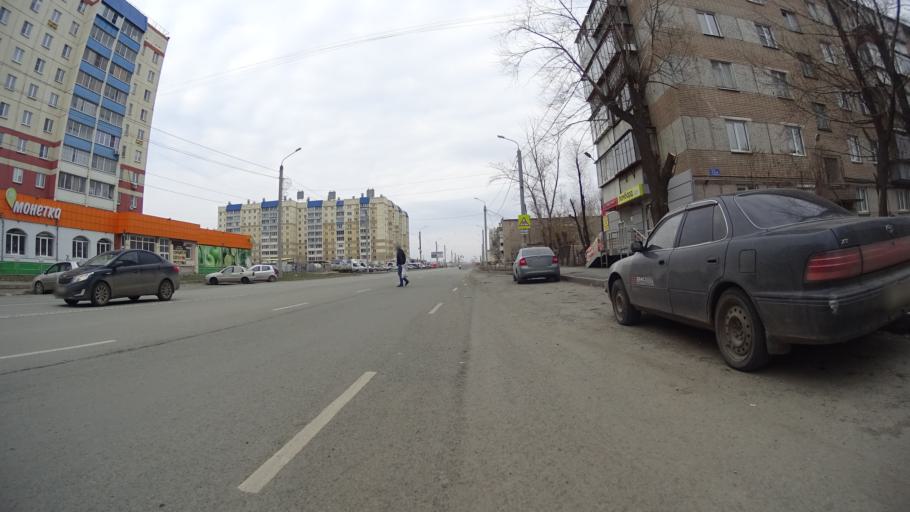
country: RU
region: Chelyabinsk
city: Zheleznodorozhnyy
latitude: 55.1691
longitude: 61.5299
